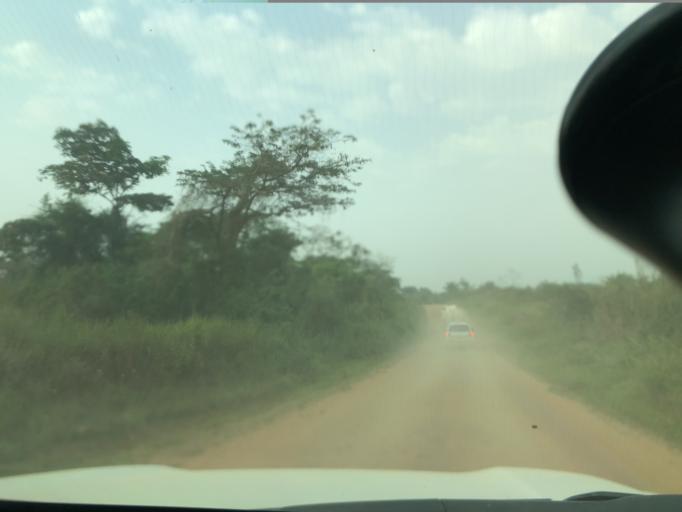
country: UG
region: Western Region
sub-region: Kasese District
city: Margherita
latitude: 0.2134
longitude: 29.6780
